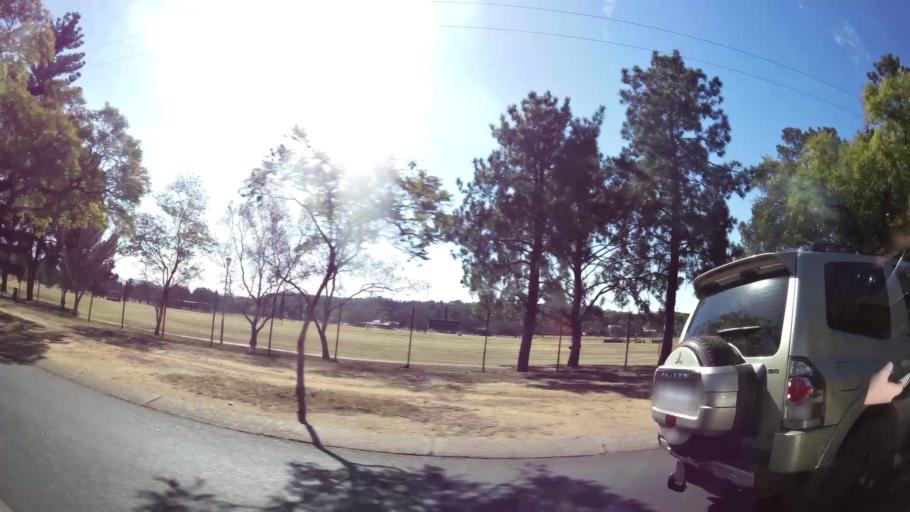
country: ZA
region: Gauteng
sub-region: City of Tshwane Metropolitan Municipality
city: Pretoria
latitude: -25.7338
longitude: 28.2231
